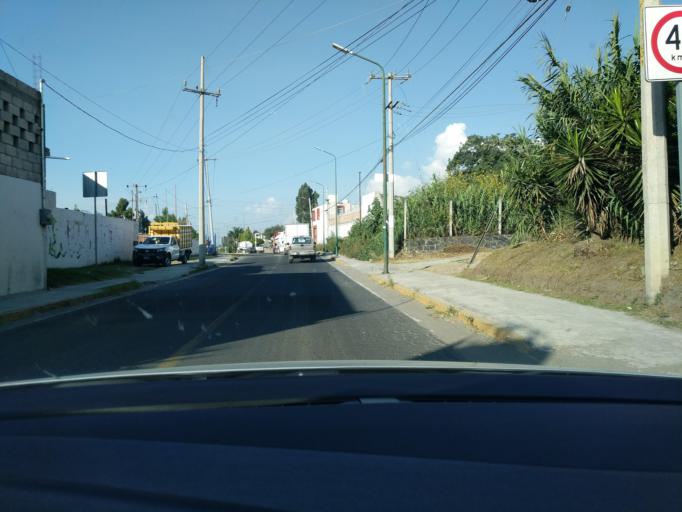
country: MX
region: Puebla
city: San Andres Cholula
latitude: 19.0345
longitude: -98.3171
